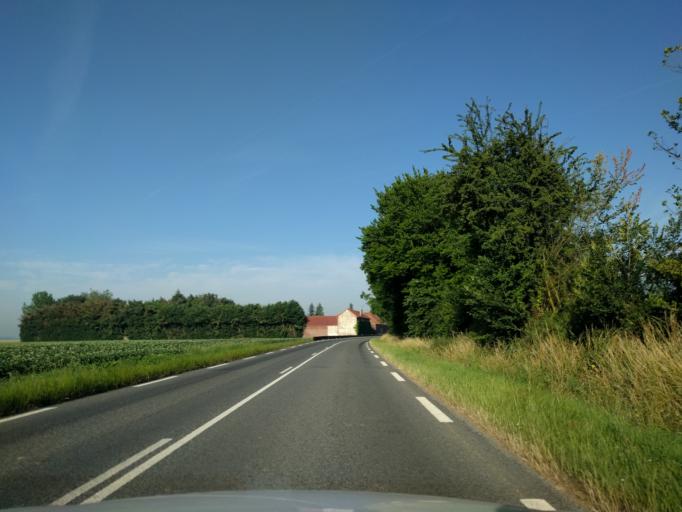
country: FR
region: Picardie
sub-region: Departement de la Somme
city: Montdidier
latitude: 49.6459
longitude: 2.6218
